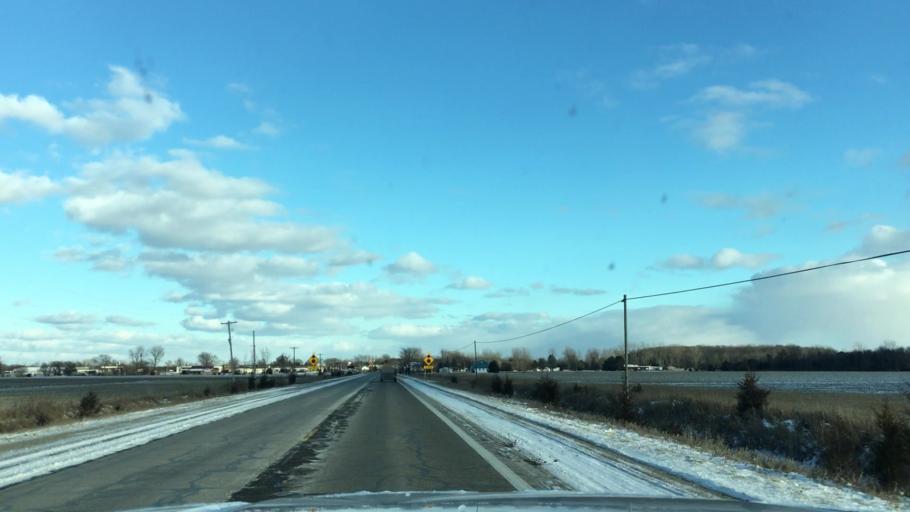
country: US
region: Michigan
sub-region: Saginaw County
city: Chesaning
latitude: 43.1866
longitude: -84.1782
